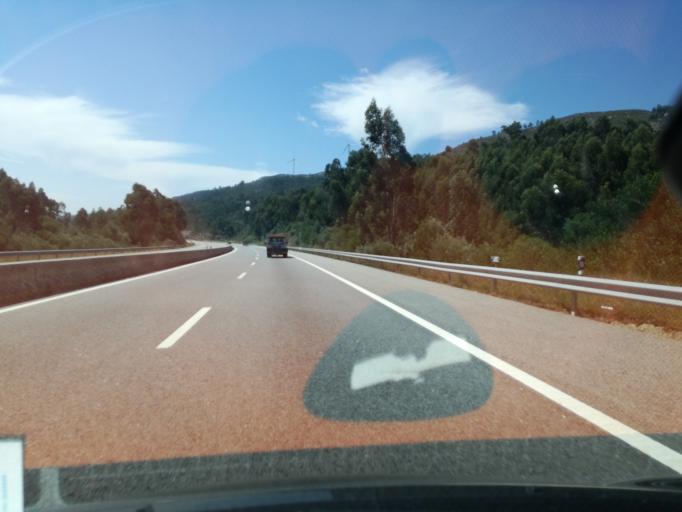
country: PT
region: Viana do Castelo
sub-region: Viana do Castelo
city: Meadela
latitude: 41.7667
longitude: -8.7906
